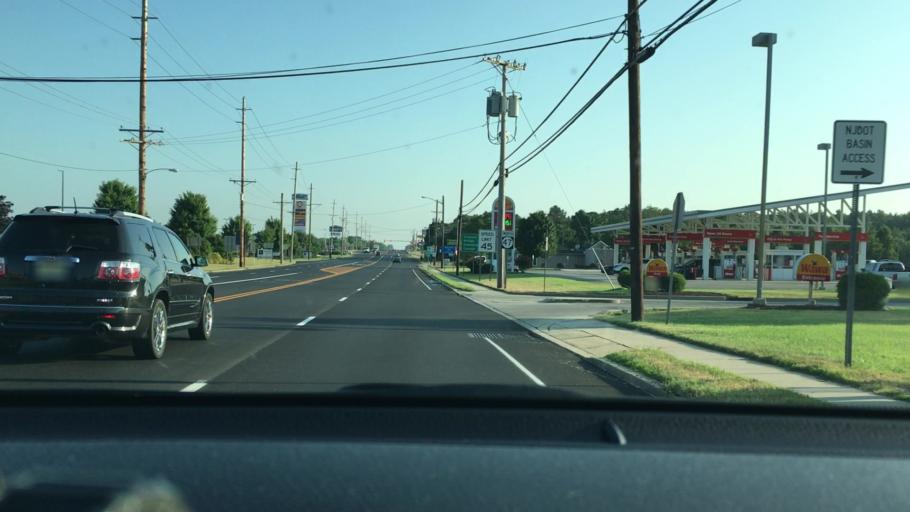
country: US
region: New Jersey
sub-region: Cumberland County
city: Millville
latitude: 39.4206
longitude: -75.0393
